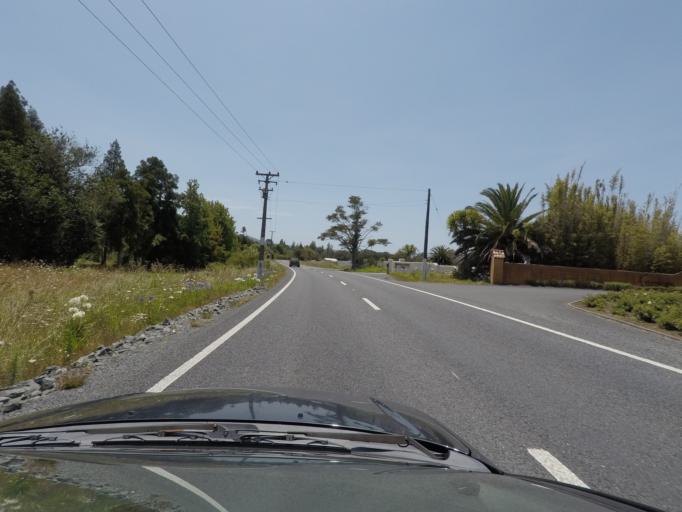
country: NZ
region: Auckland
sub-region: Auckland
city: Warkworth
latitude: -36.3720
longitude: 174.6806
